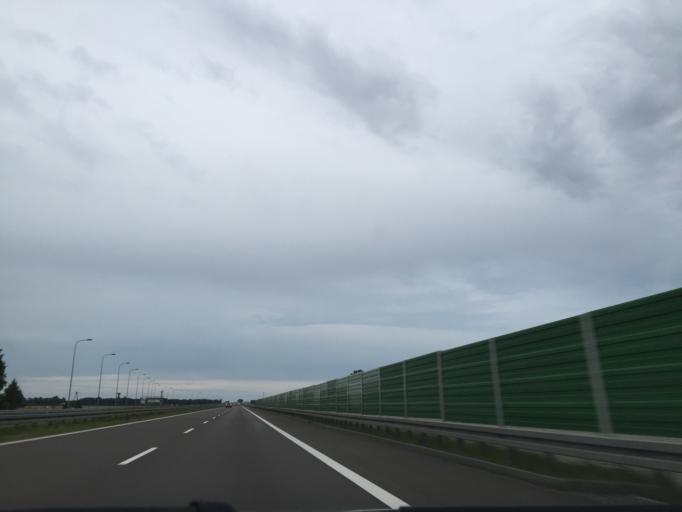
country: PL
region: Podlasie
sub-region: Powiat bialostocki
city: Choroszcz
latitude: 53.1579
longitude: 22.8841
